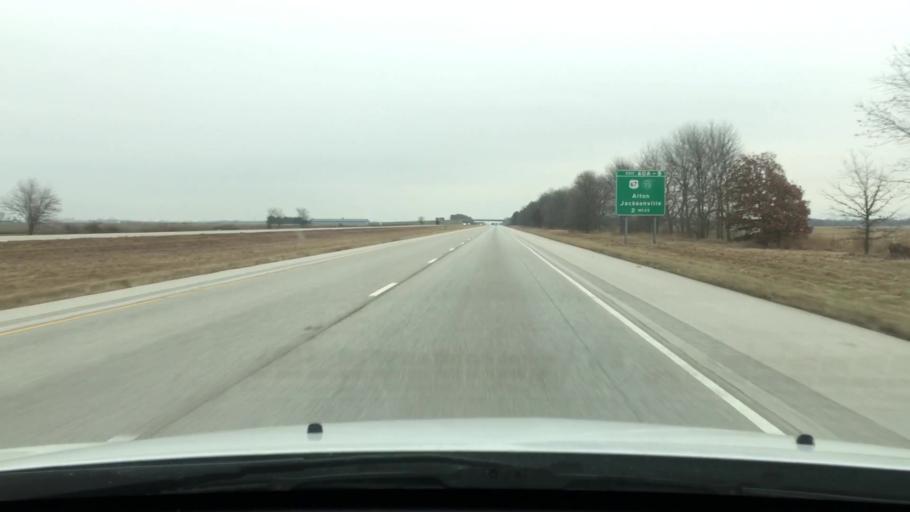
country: US
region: Illinois
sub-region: Morgan County
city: South Jacksonville
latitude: 39.6802
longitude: -90.3418
